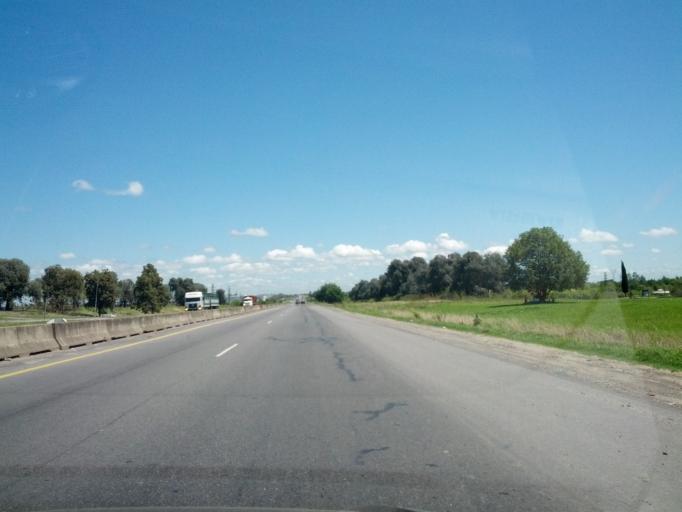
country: AR
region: Buenos Aires
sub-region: Partido de Zarate
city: Zarate
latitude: -34.1237
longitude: -59.0221
